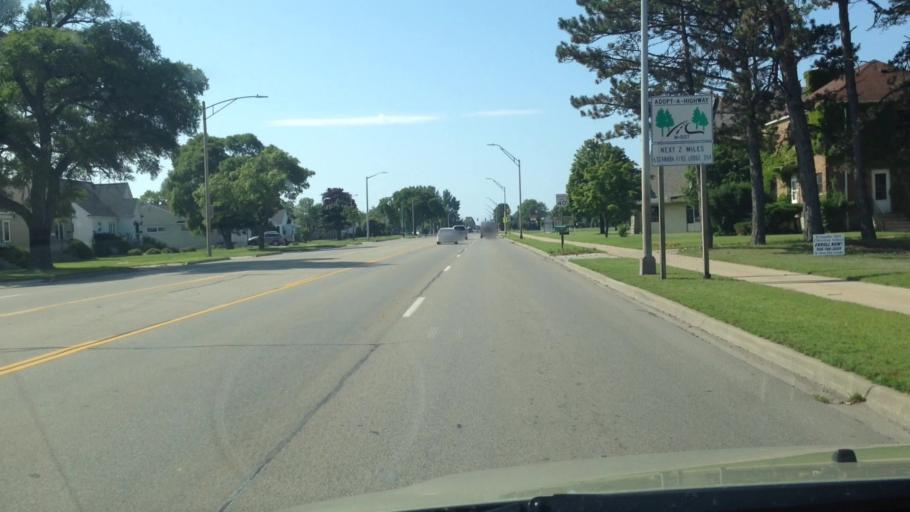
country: US
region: Michigan
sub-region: Delta County
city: Escanaba
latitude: 45.7439
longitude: -87.0799
